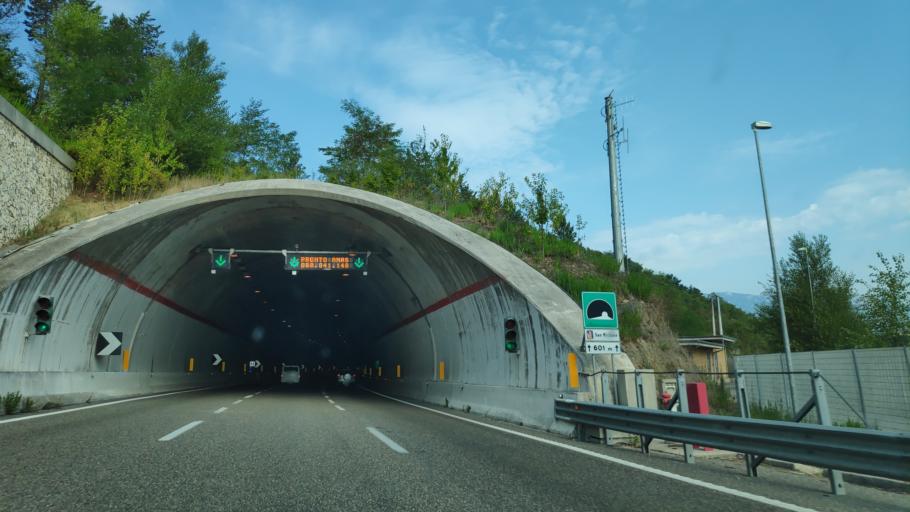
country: IT
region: Campania
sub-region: Provincia di Salerno
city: Contursi Terme
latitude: 40.6134
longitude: 15.2509
